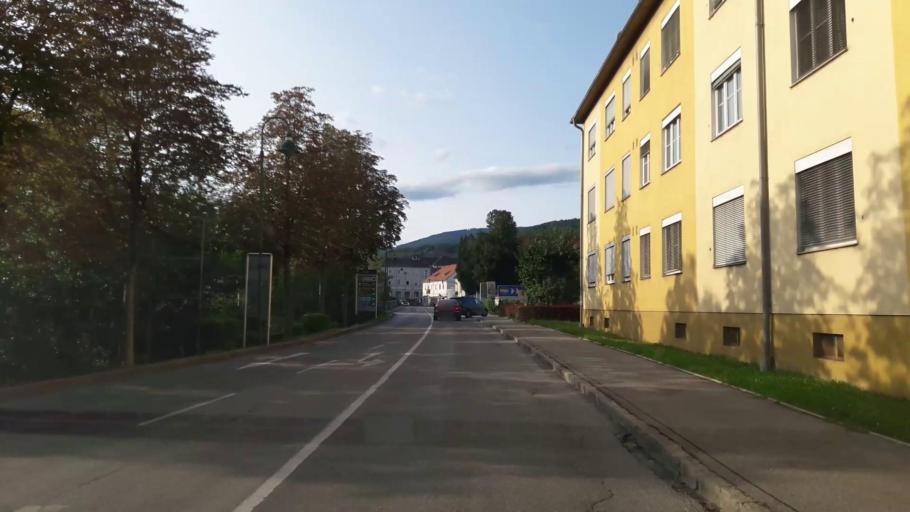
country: AT
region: Styria
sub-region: Politischer Bezirk Weiz
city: Weiz
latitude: 47.2155
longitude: 15.6273
